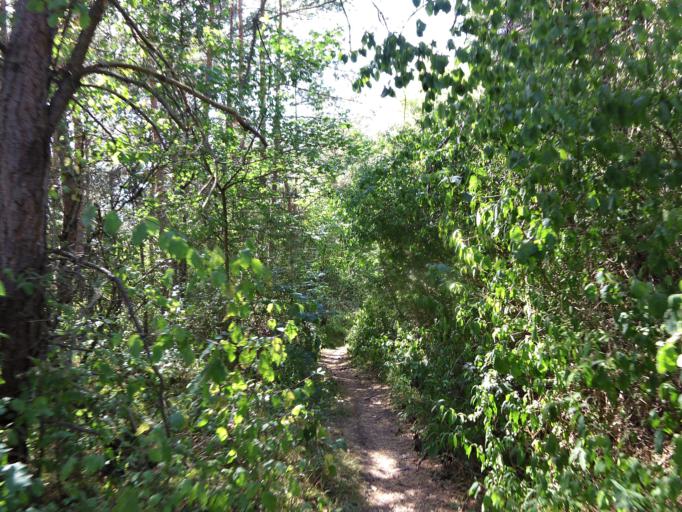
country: DE
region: Bavaria
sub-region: Regierungsbezirk Unterfranken
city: Eibelstadt
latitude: 49.7435
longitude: 10.0056
